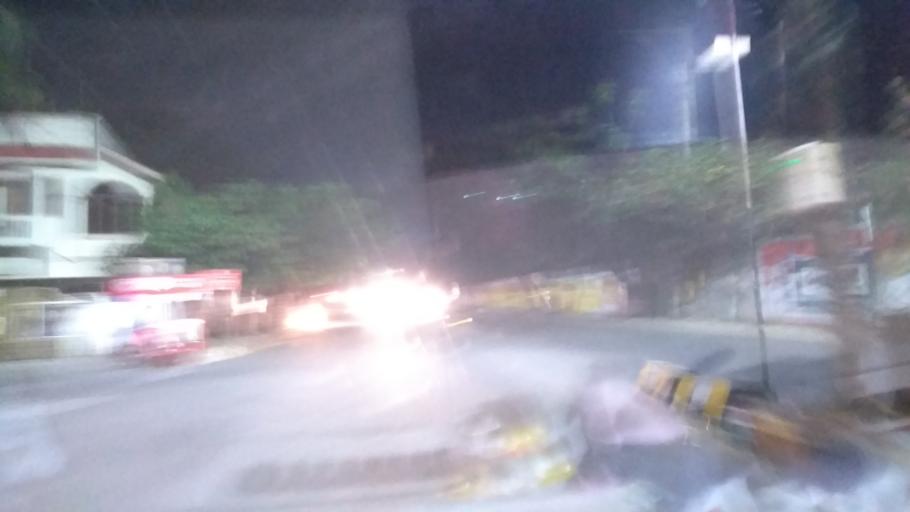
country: IN
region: Telangana
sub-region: Rangareddi
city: Kukatpalli
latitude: 17.4435
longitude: 78.4361
